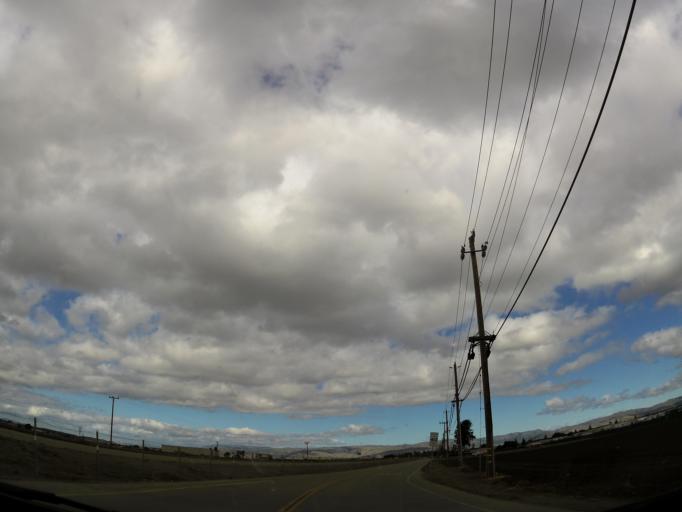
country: US
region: California
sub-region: San Benito County
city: Hollister
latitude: 36.8759
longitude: -121.4003
